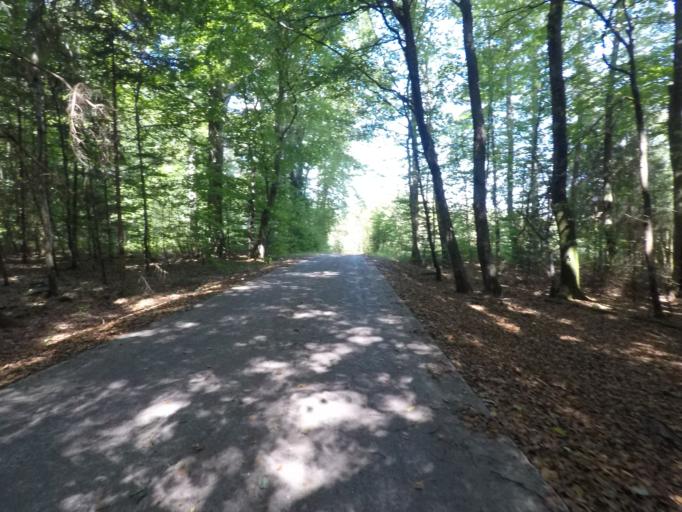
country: LU
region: Luxembourg
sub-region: Canton de Capellen
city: Garnich
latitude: 49.6320
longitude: 5.9464
